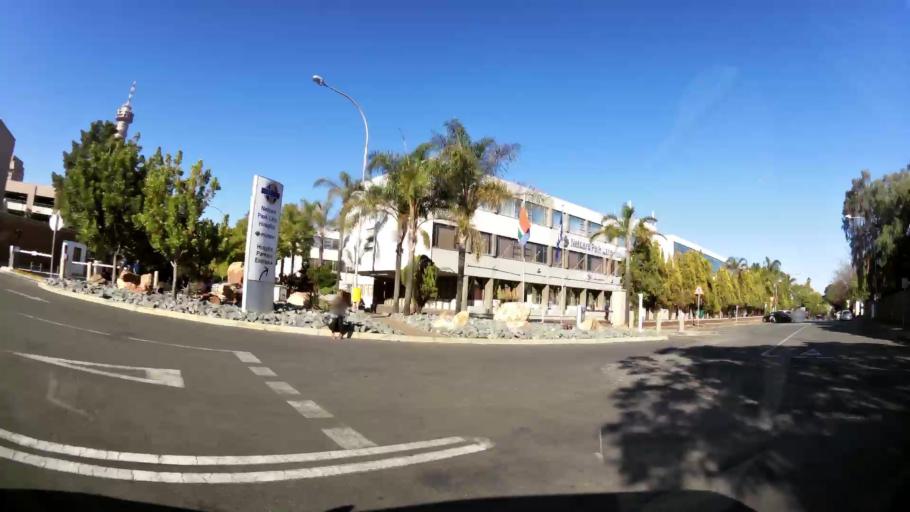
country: ZA
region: Gauteng
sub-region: City of Johannesburg Metropolitan Municipality
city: Johannesburg
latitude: -26.1815
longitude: 28.0468
